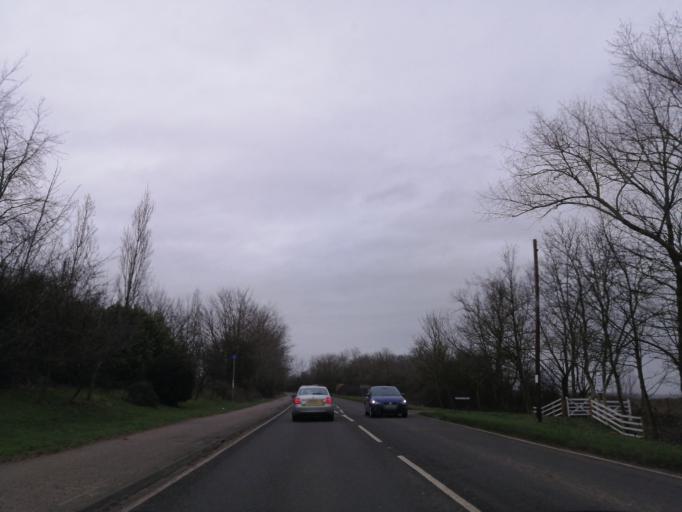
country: GB
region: England
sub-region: Cambridgeshire
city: Stilton
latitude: 52.5060
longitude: -0.2845
